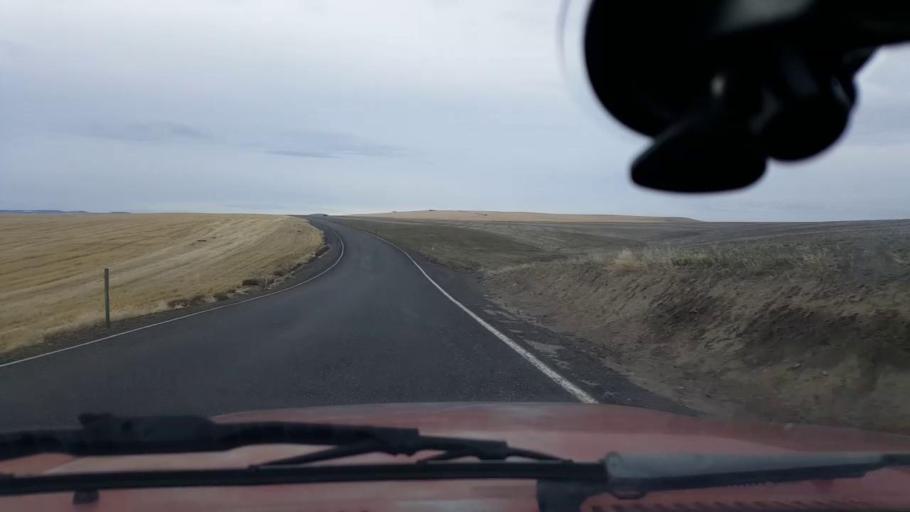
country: US
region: Washington
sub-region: Asotin County
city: Clarkston Heights-Vineland
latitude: 46.3560
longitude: -117.2221
